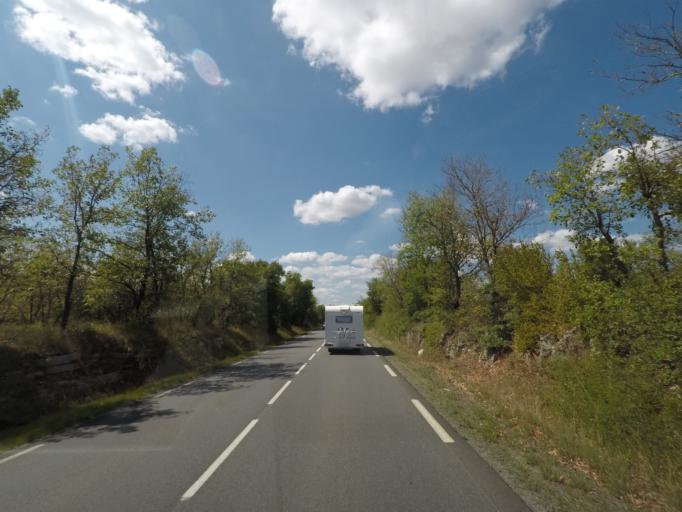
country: FR
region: Midi-Pyrenees
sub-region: Departement du Lot
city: Lacapelle-Marival
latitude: 44.6269
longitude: 1.8872
